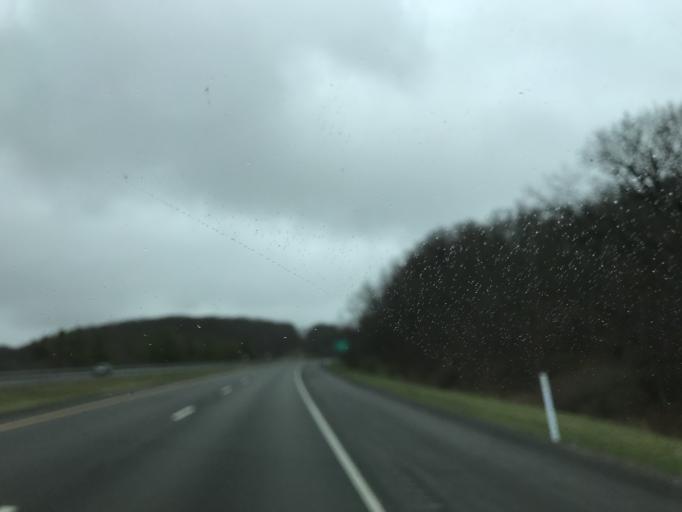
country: US
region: West Virginia
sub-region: Greenbrier County
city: Rainelle
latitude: 37.9052
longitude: -80.6028
